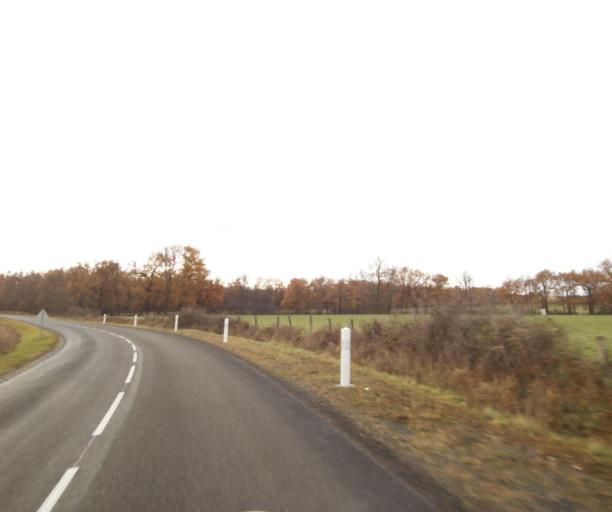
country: FR
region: Rhone-Alpes
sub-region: Departement de la Loire
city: Saint-Romain-le-Puy
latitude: 45.5351
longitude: 4.1504
